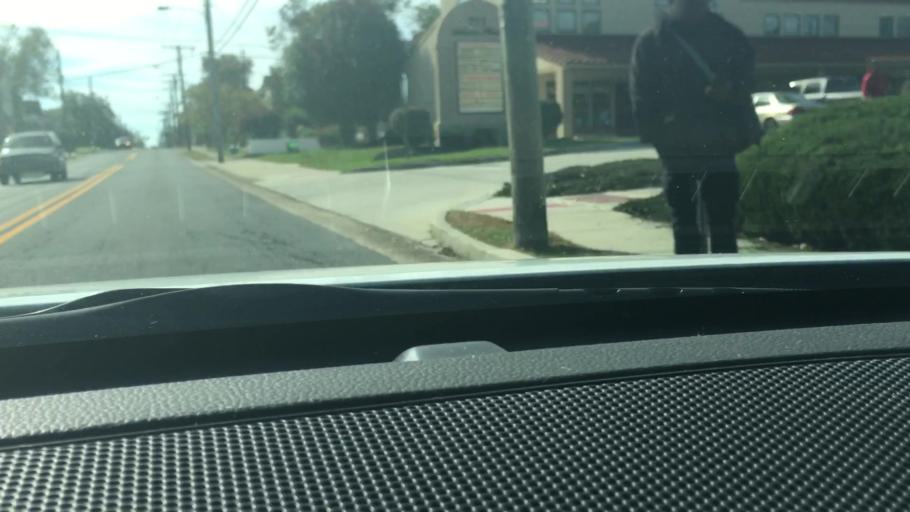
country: US
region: New Jersey
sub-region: Atlantic County
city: Pleasantville
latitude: 39.4009
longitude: -74.5144
